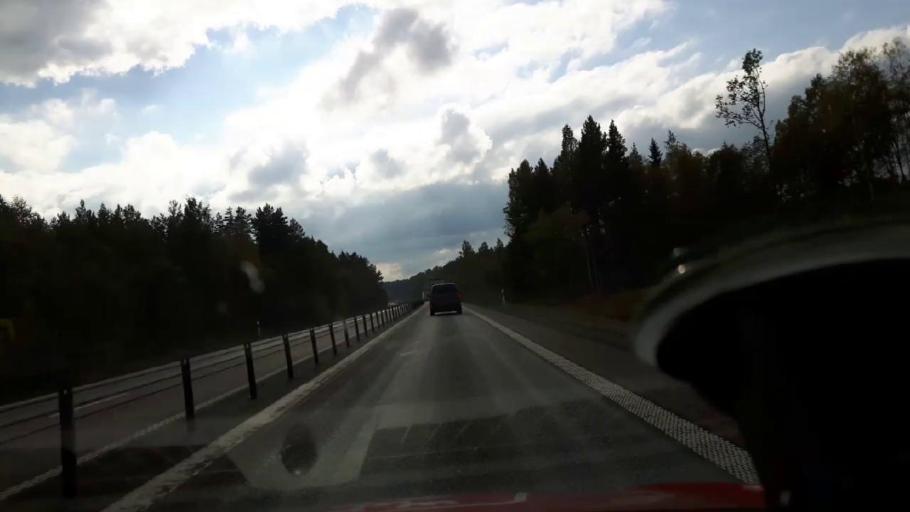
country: SE
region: Gaevleborg
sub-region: Gavle Kommun
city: Norrsundet
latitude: 60.9399
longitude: 17.0180
